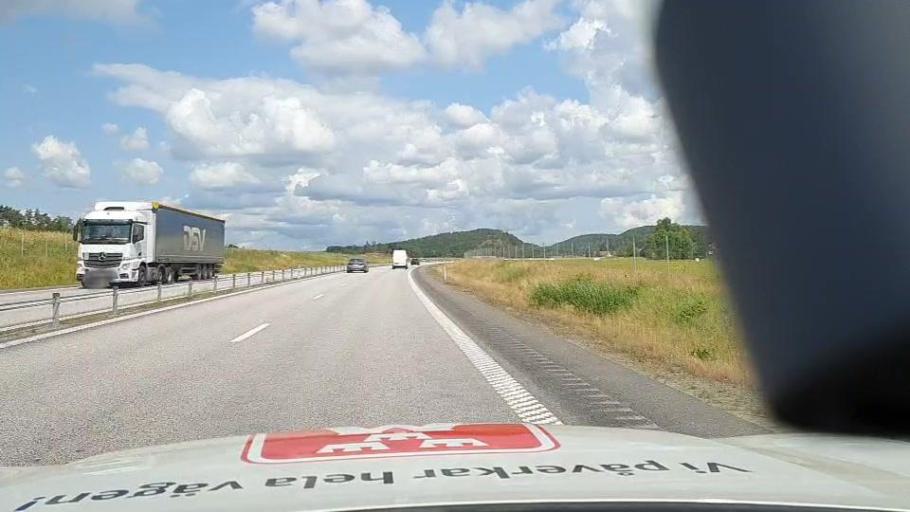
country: SE
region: Vaestra Goetaland
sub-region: Lilla Edets Kommun
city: Lodose
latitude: 58.0753
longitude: 12.1546
